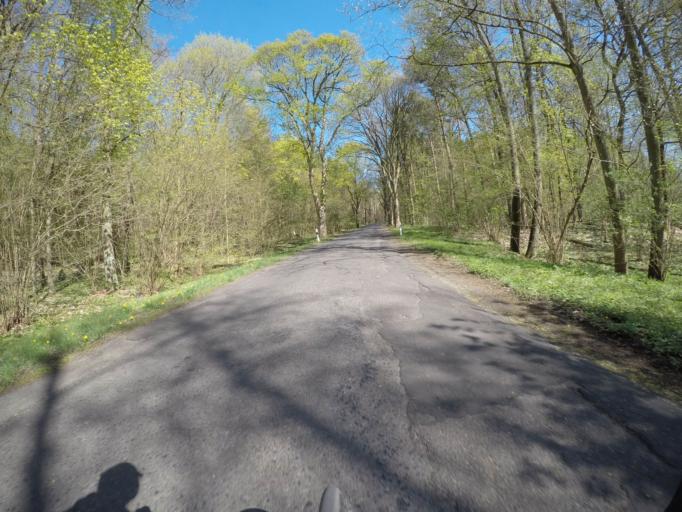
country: DE
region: Brandenburg
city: Werftpfuhl
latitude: 52.6204
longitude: 13.8363
